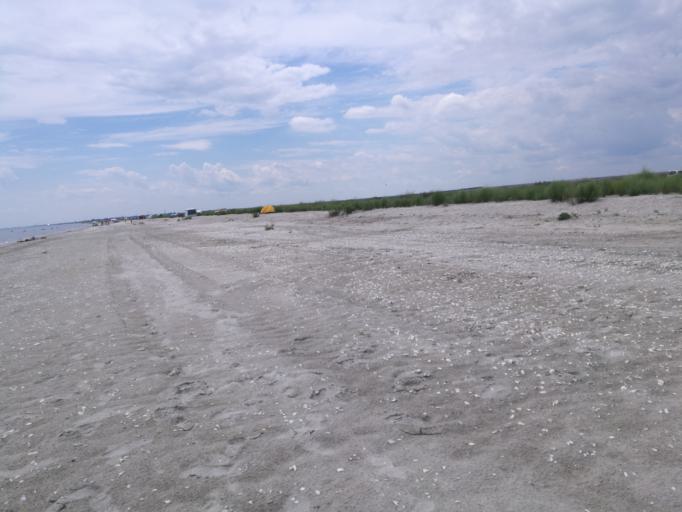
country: RO
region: Constanta
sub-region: Comuna Corbu
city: Corbu
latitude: 44.4263
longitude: 28.7632
